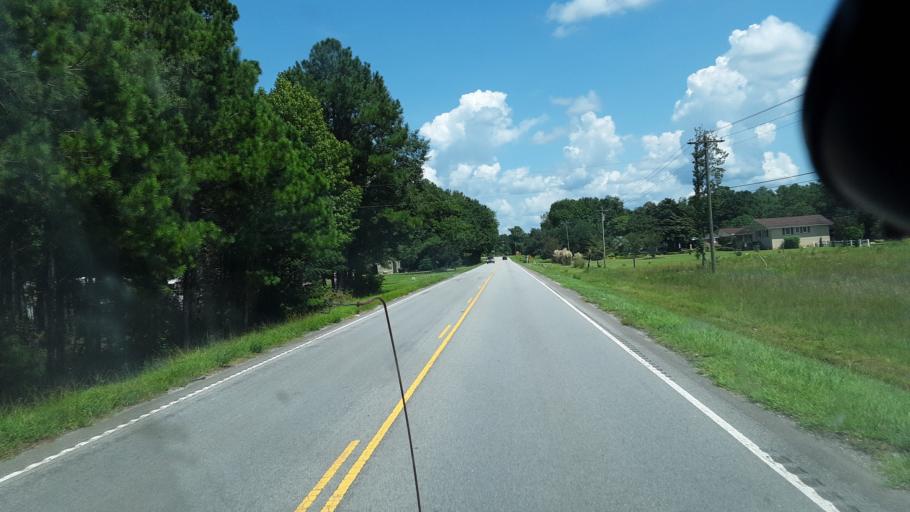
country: US
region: South Carolina
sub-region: Berkeley County
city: Moncks Corner
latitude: 33.2361
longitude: -79.9460
